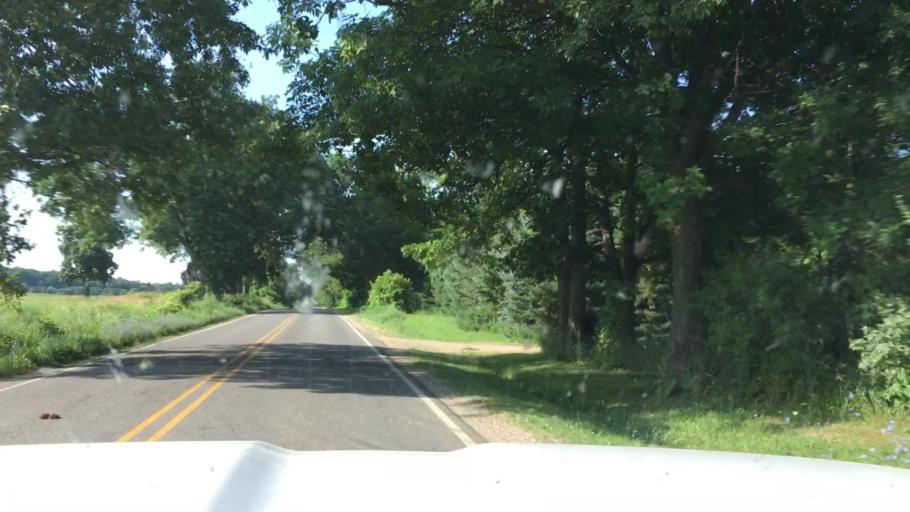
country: US
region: Michigan
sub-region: Barry County
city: Stony Point
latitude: 42.4477
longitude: -85.4544
